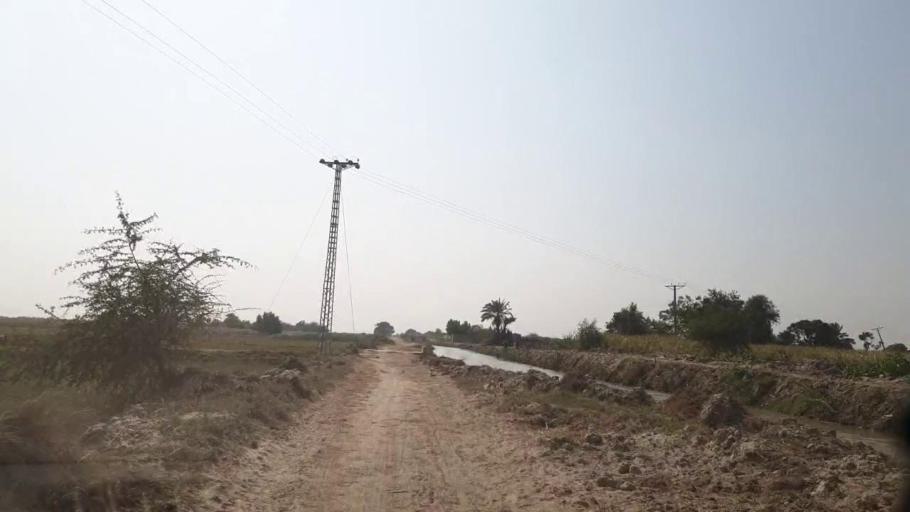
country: PK
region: Sindh
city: Bulri
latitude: 24.9609
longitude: 68.3895
